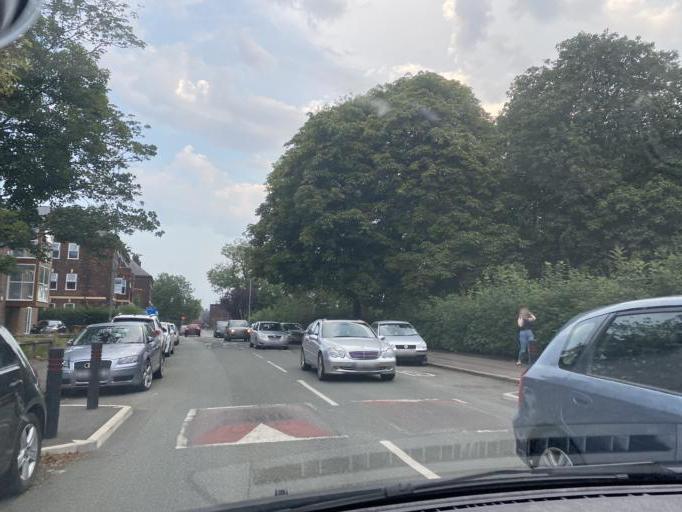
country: GB
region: England
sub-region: Manchester
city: Fallowfield
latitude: 53.4509
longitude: -2.2238
